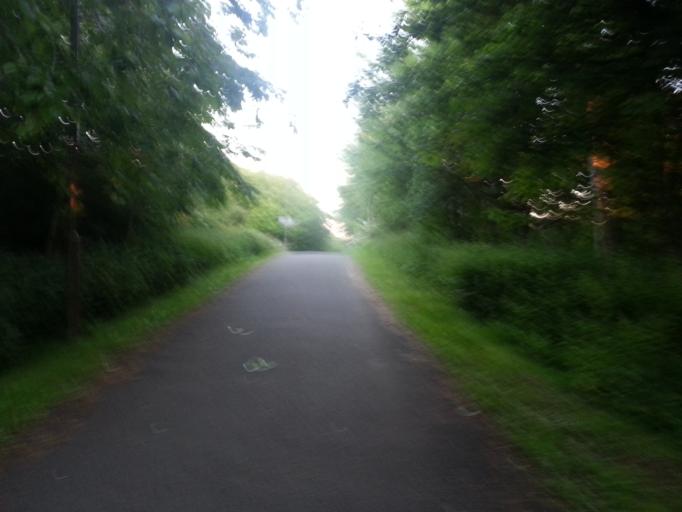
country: GB
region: Scotland
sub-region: West Lothian
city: Seafield
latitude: 55.9263
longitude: -3.1380
